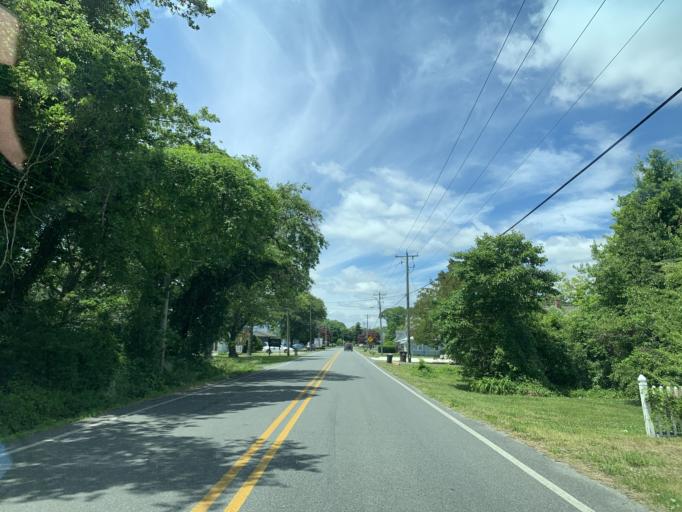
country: US
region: Maryland
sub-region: Worcester County
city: West Ocean City
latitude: 38.3321
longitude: -75.1097
